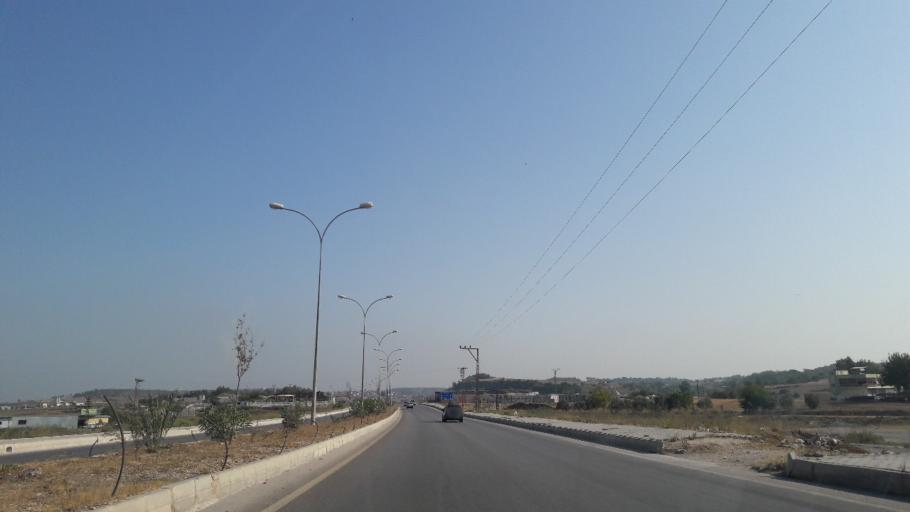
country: TR
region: Adana
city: Yuregir
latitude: 37.0484
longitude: 35.4376
